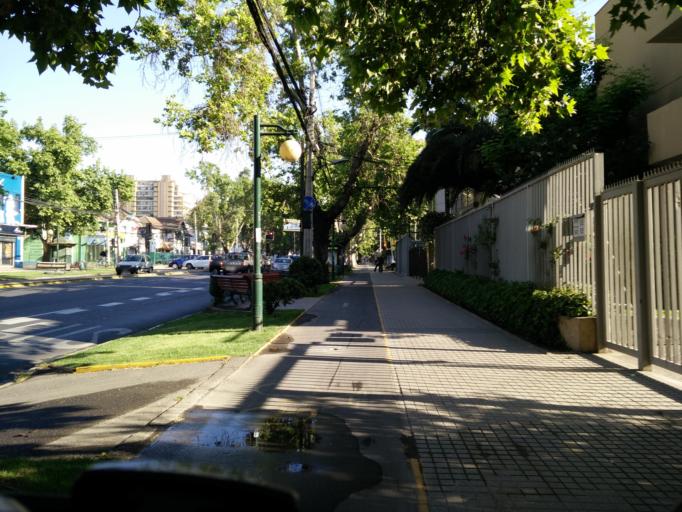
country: CL
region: Santiago Metropolitan
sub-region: Provincia de Santiago
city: Villa Presidente Frei, Nunoa, Santiago, Chile
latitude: -33.4493
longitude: -70.6054
